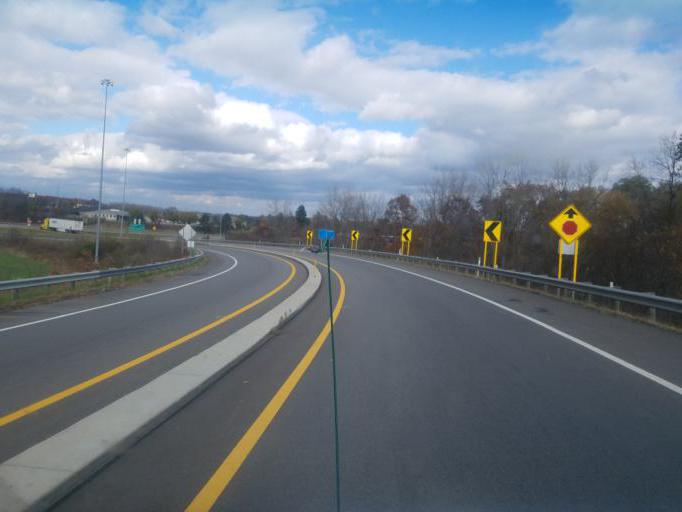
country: US
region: Ohio
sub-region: Richland County
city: Lincoln Heights
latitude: 40.7809
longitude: -82.4101
